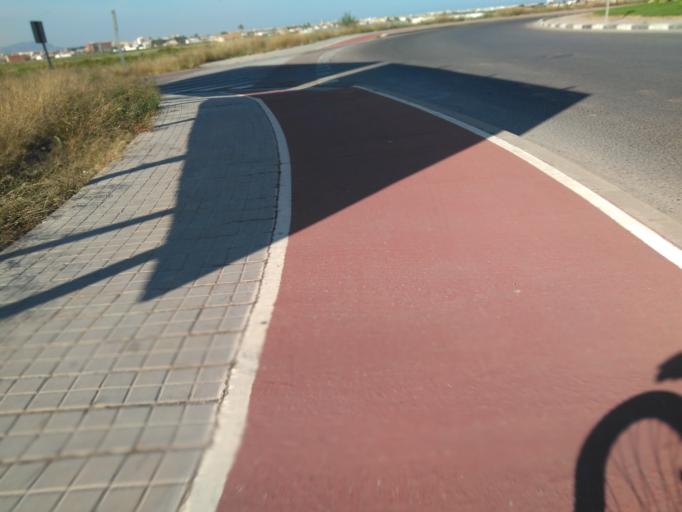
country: ES
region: Valencia
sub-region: Provincia de Valencia
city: Burjassot
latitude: 39.5034
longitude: -0.3993
